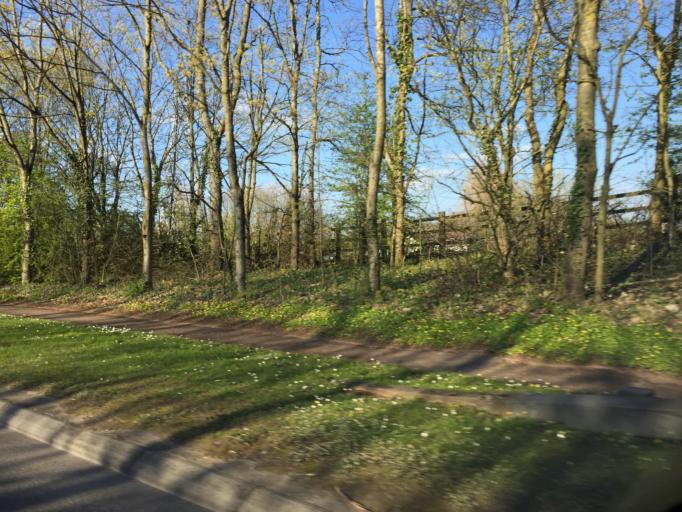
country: GB
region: Wales
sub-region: Torfaen County Borough
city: Cwmbran
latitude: 51.6301
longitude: -3.0186
